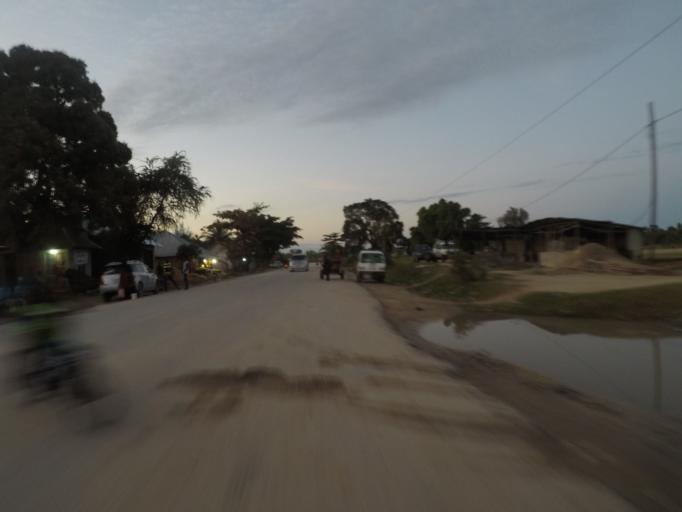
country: TZ
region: Zanzibar Central/South
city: Koani
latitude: -6.0798
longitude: 39.2221
